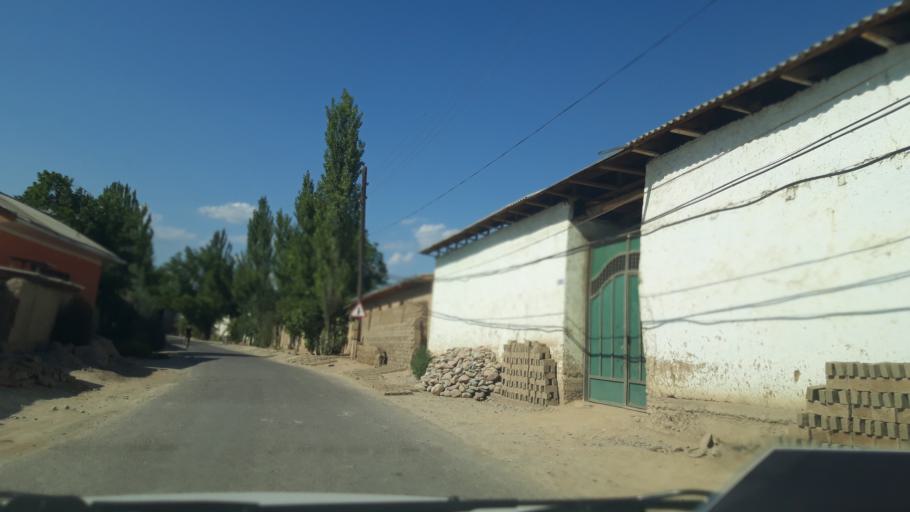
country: UZ
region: Namangan
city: Yangiqo`rg`on
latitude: 41.2042
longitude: 71.7262
